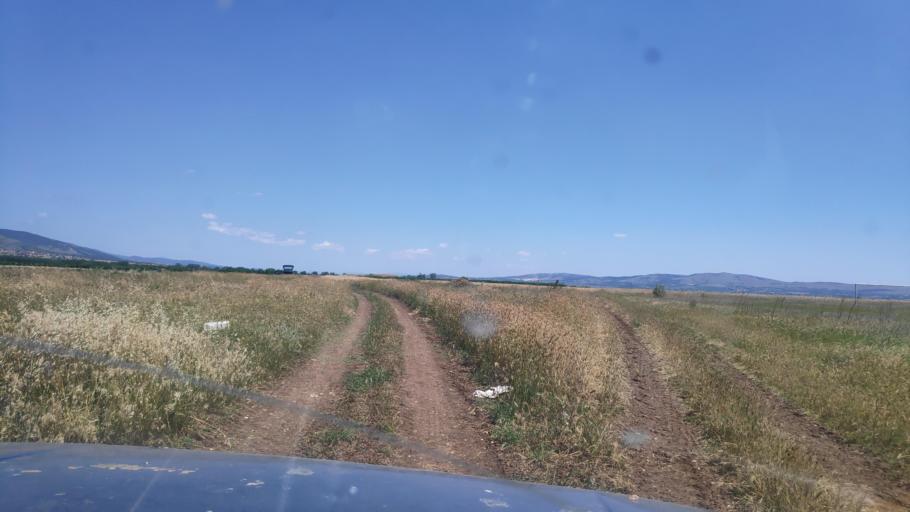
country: MK
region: Kumanovo
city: Bedinje
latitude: 42.1631
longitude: 21.6837
